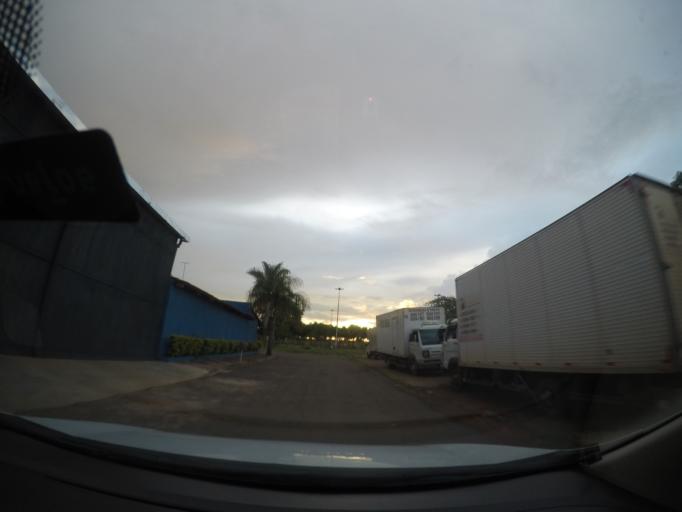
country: BR
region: Goias
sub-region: Goiania
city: Goiania
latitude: -16.7249
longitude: -49.3702
